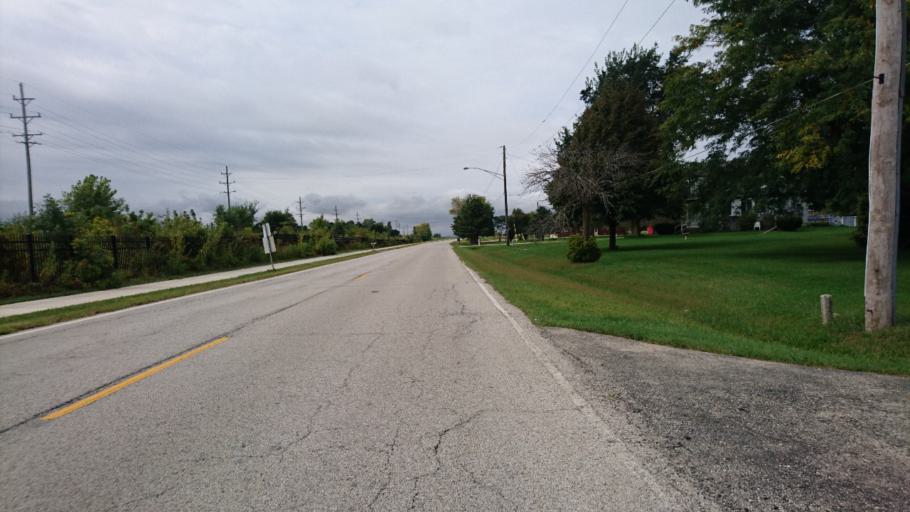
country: US
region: Illinois
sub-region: Livingston County
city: Dwight
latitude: 41.0830
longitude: -88.4403
